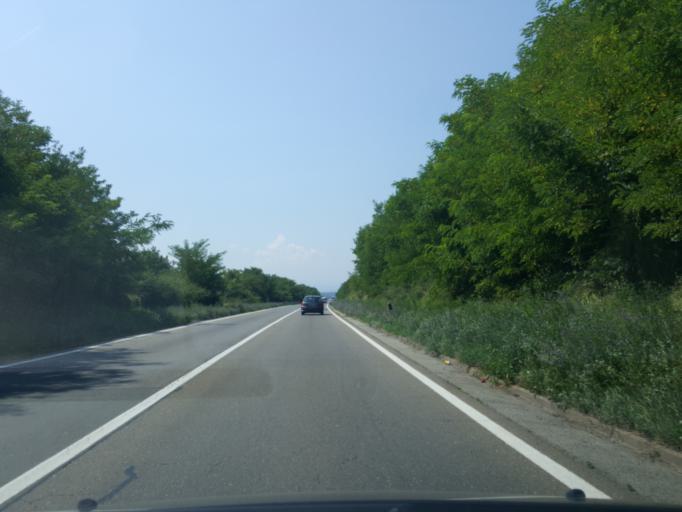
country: RS
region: Central Serbia
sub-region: Belgrade
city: Sopot
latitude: 44.5254
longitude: 20.6551
